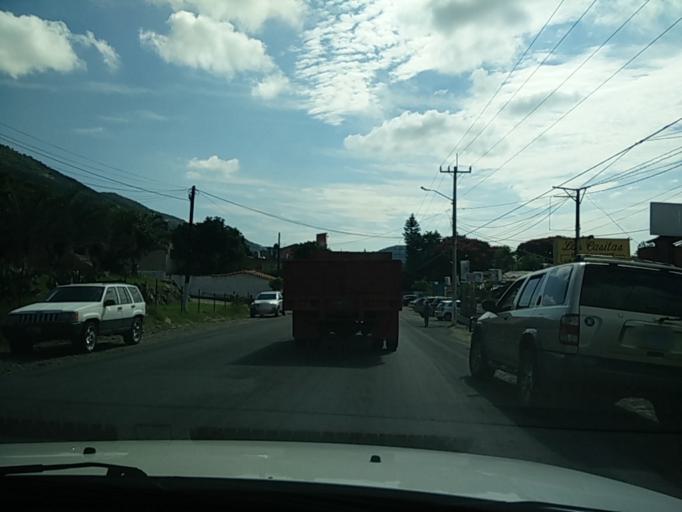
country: MX
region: Jalisco
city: Ajijic
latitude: 20.3015
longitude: -103.2649
